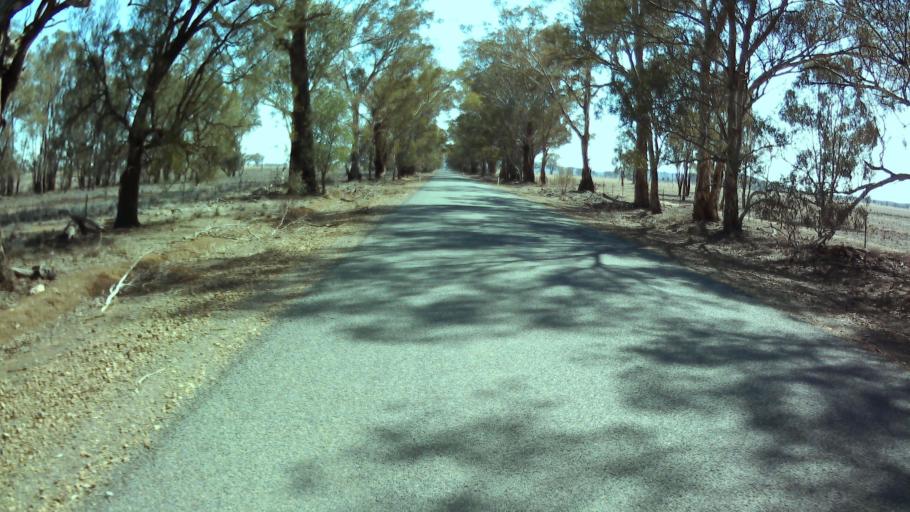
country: AU
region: New South Wales
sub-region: Weddin
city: Grenfell
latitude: -33.7248
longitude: 147.8950
